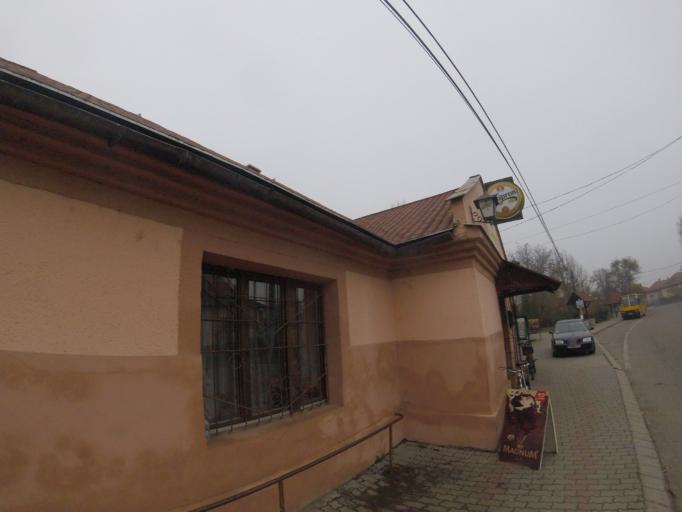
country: HU
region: Heves
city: Szilvasvarad
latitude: 48.1743
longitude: 20.4867
